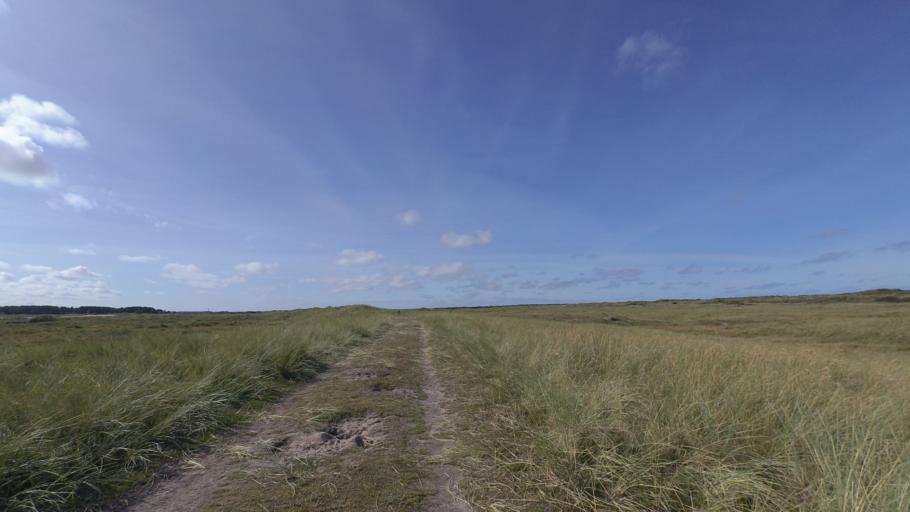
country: NL
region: Friesland
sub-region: Gemeente Ameland
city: Nes
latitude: 53.4547
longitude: 5.7075
